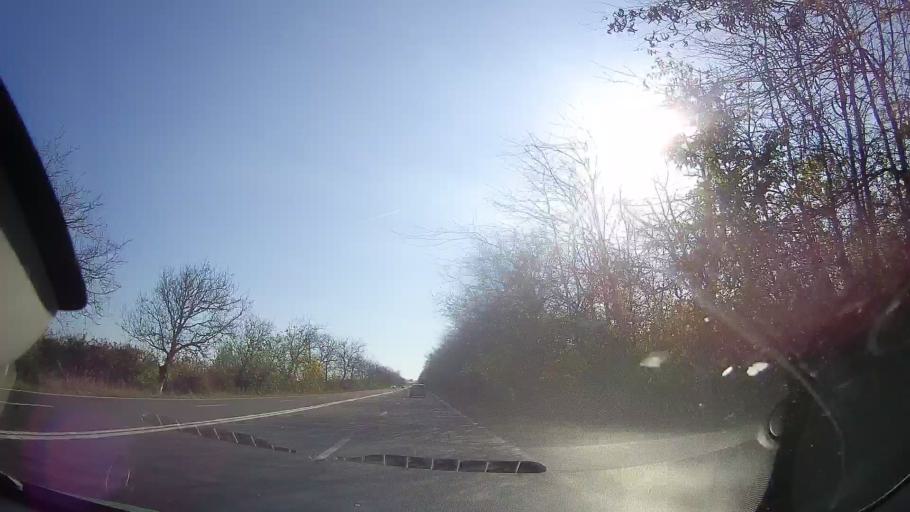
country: RO
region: Constanta
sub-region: Comuna Douazeci si Trei August
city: Douazeci si Trei August
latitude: 43.8928
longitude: 28.5720
